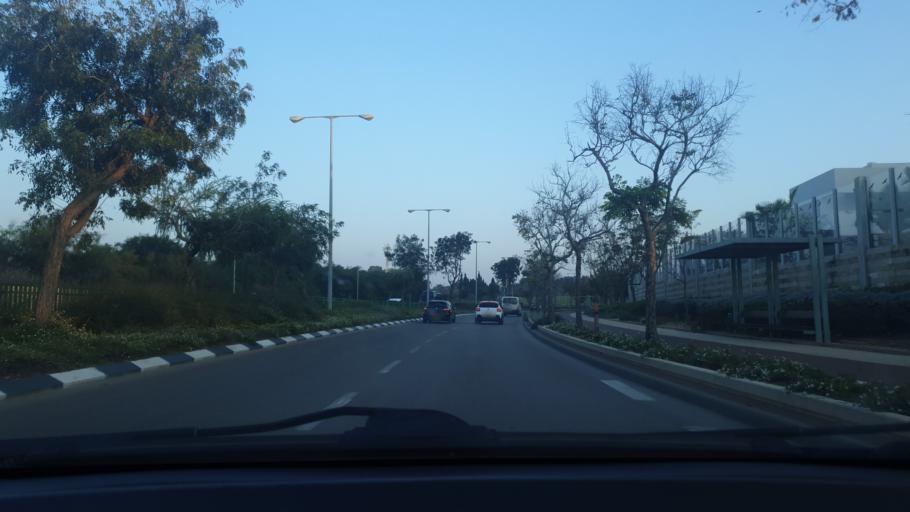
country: IL
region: Central District
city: Bet Dagan
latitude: 31.9709
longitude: 34.8243
